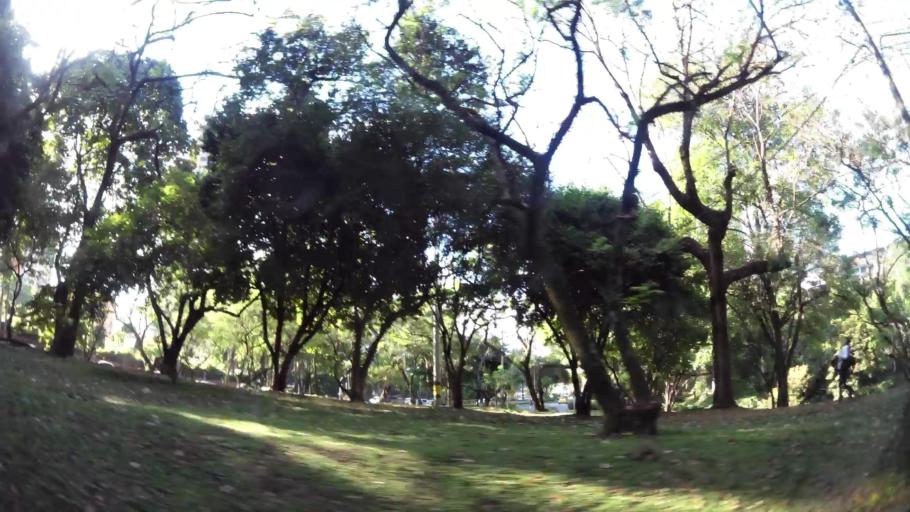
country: CO
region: Antioquia
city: Envigado
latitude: 6.1923
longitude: -75.5759
